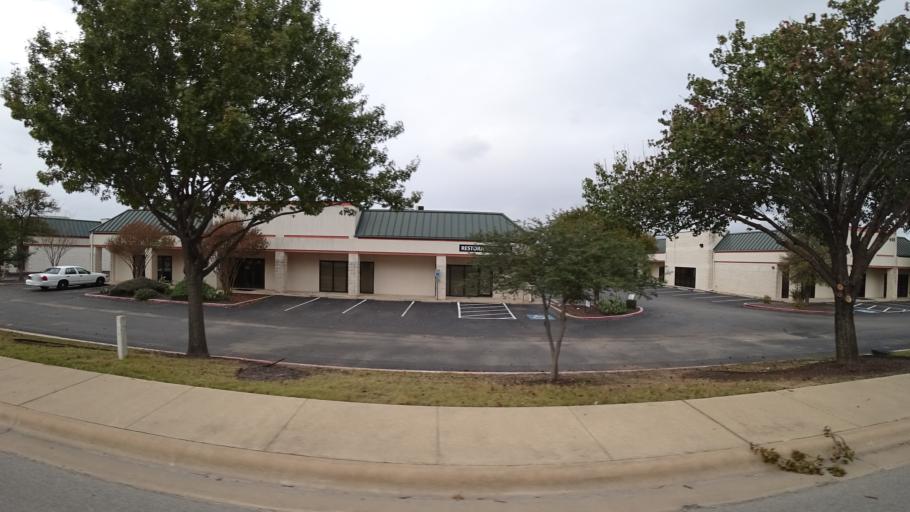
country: US
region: Texas
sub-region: Williamson County
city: Round Rock
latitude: 30.5035
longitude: -97.6927
